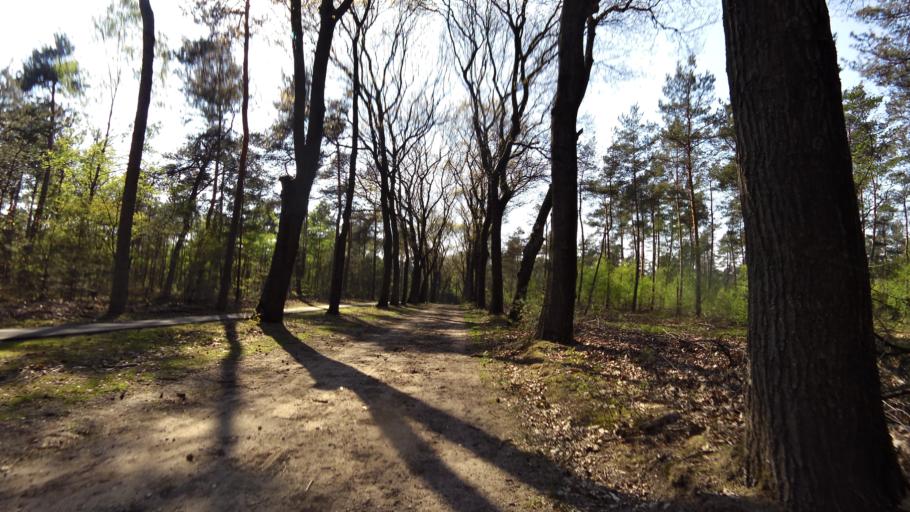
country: NL
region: Gelderland
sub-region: Gemeente Arnhem
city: Gulden Bodem
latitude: 52.0147
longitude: 5.8897
